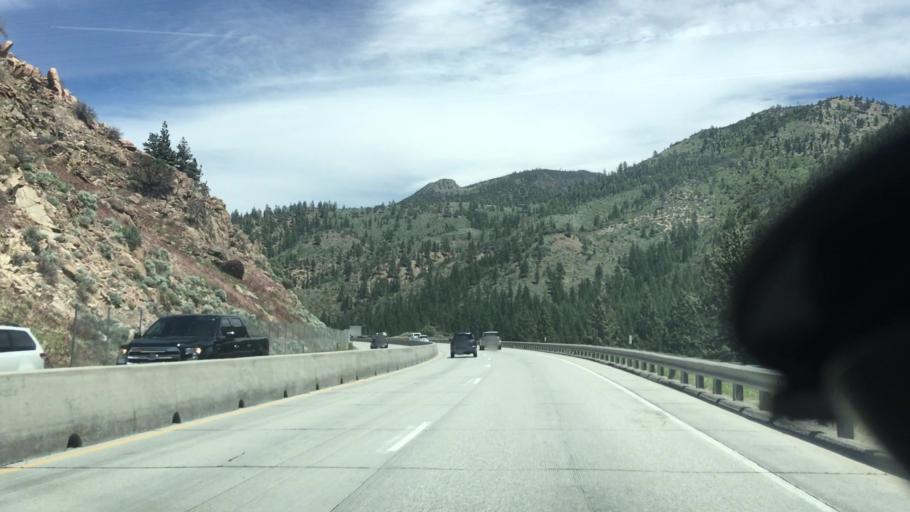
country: US
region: Nevada
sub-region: Washoe County
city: Verdi
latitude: 39.4416
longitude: -120.0147
